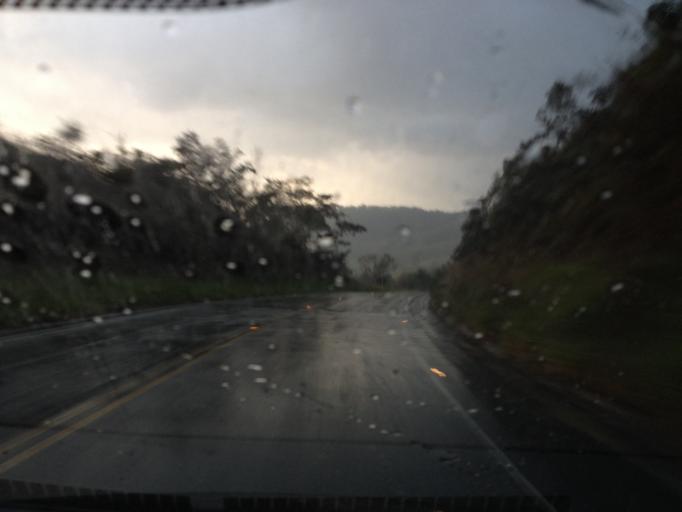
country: BR
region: Minas Gerais
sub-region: Caxambu
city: Caxambu
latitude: -21.9831
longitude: -44.9898
